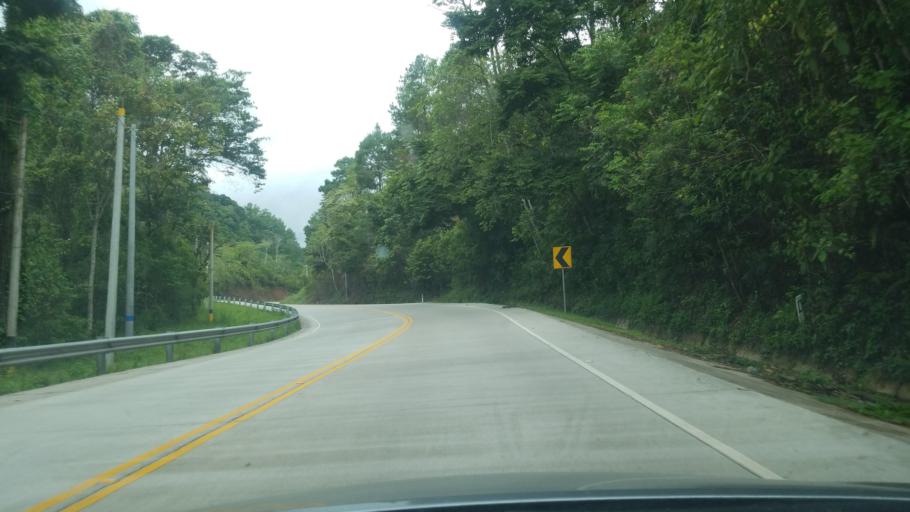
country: HN
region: Copan
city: San Jeronimo
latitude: 14.9315
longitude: -88.9442
